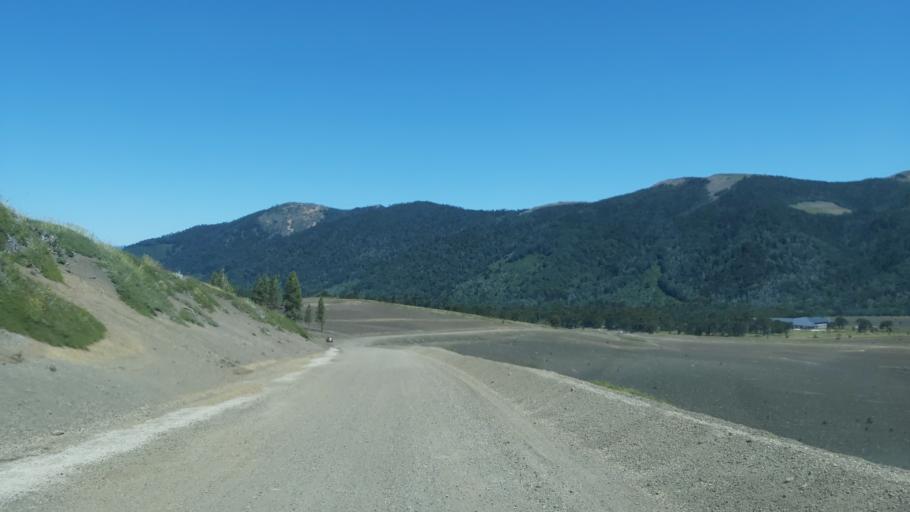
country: CL
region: Araucania
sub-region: Provincia de Cautin
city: Vilcun
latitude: -38.4124
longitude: -71.5420
